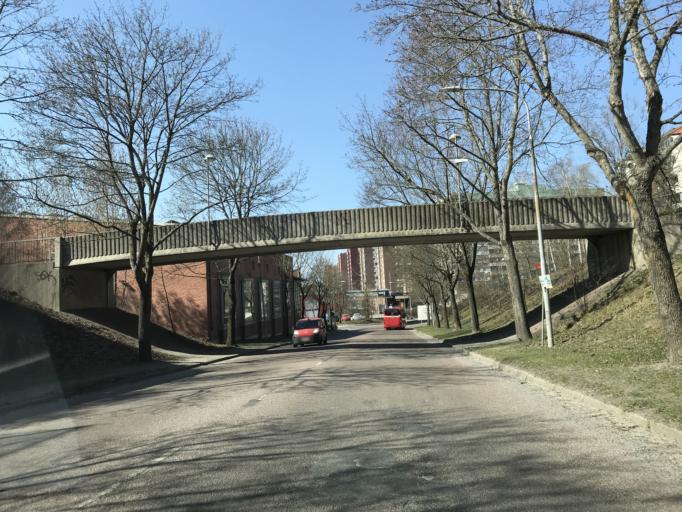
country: SE
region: Stockholm
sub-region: Stockholms Kommun
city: Kista
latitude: 59.4117
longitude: 17.9243
